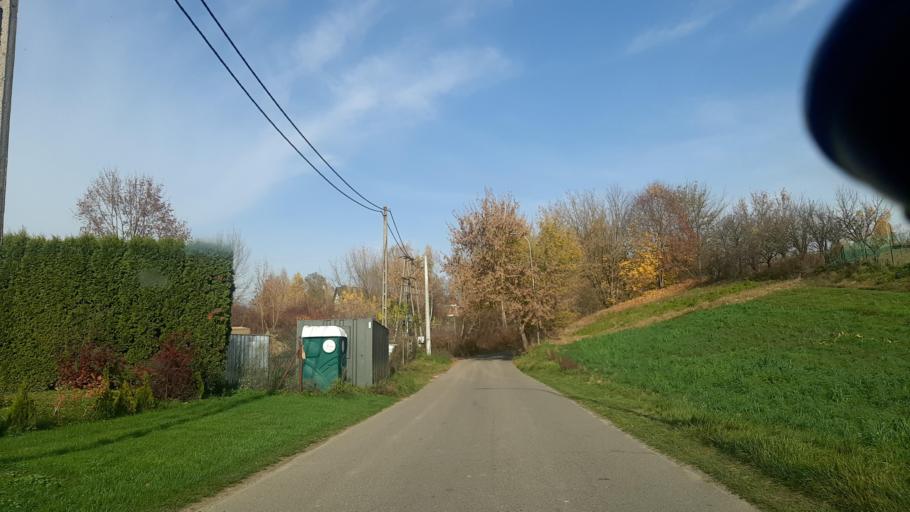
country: PL
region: Lublin Voivodeship
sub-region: Powiat lubelski
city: Lublin
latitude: 51.3165
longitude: 22.5375
